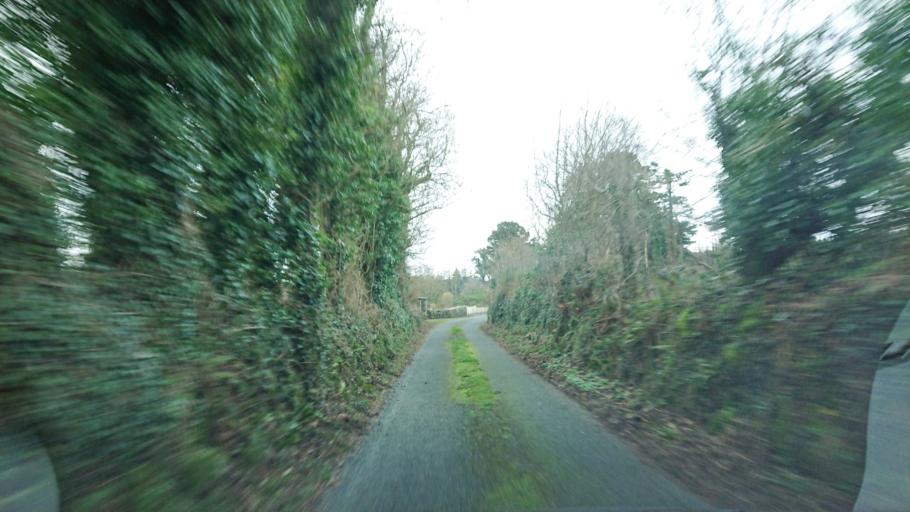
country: IE
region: Leinster
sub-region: Kilkenny
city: Mooncoin
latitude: 52.2170
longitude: -7.2712
